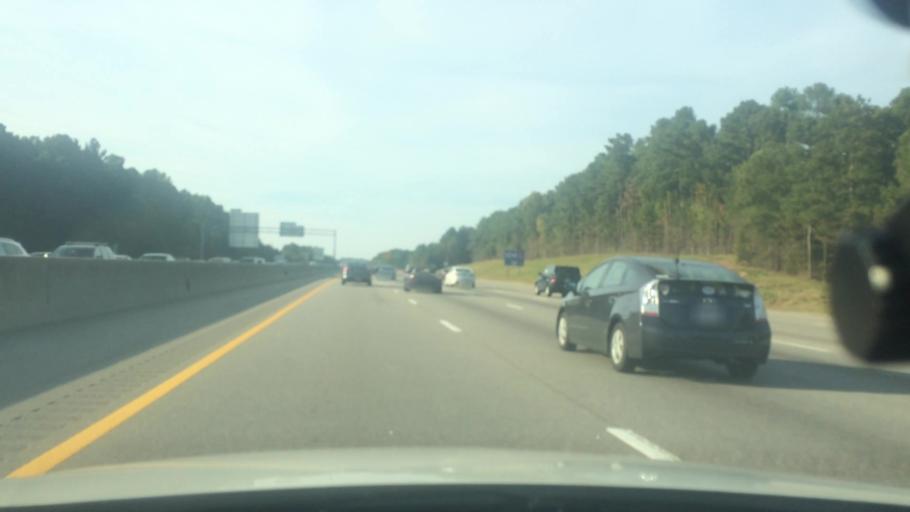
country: US
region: North Carolina
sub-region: Wake County
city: Morrisville
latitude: 35.8767
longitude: -78.8337
